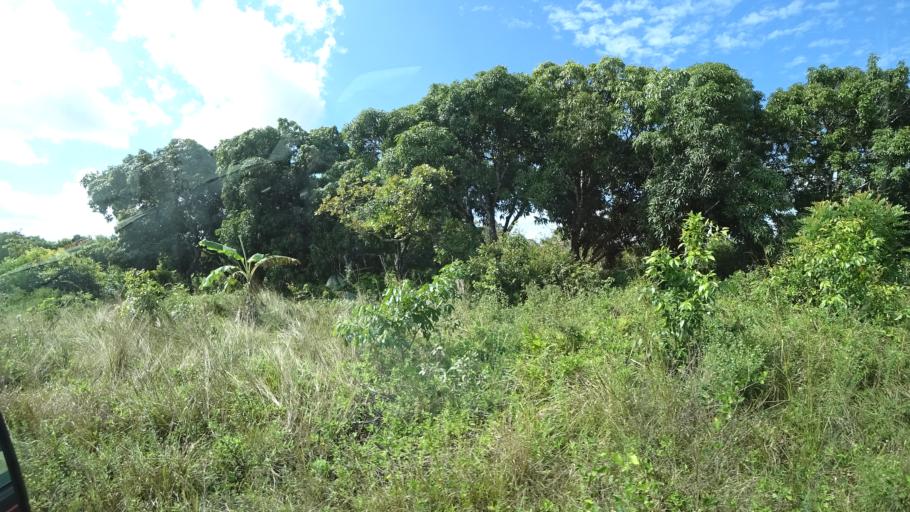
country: BZ
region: Belize
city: Belize City
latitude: 17.5700
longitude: -88.4143
